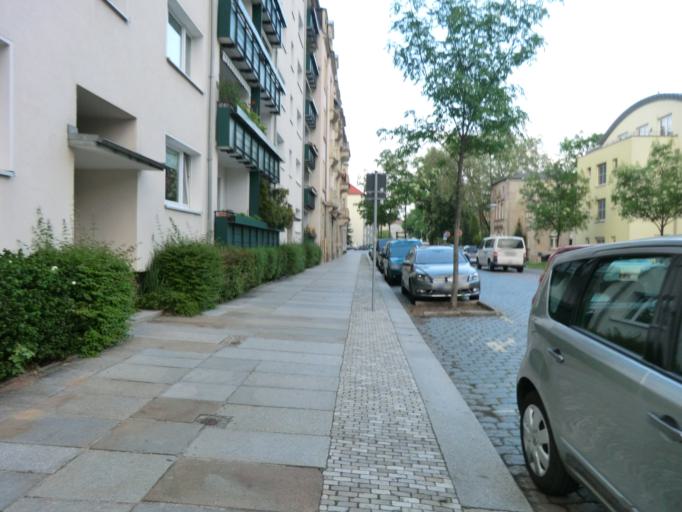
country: DE
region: Saxony
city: Albertstadt
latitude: 51.0582
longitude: 13.7677
